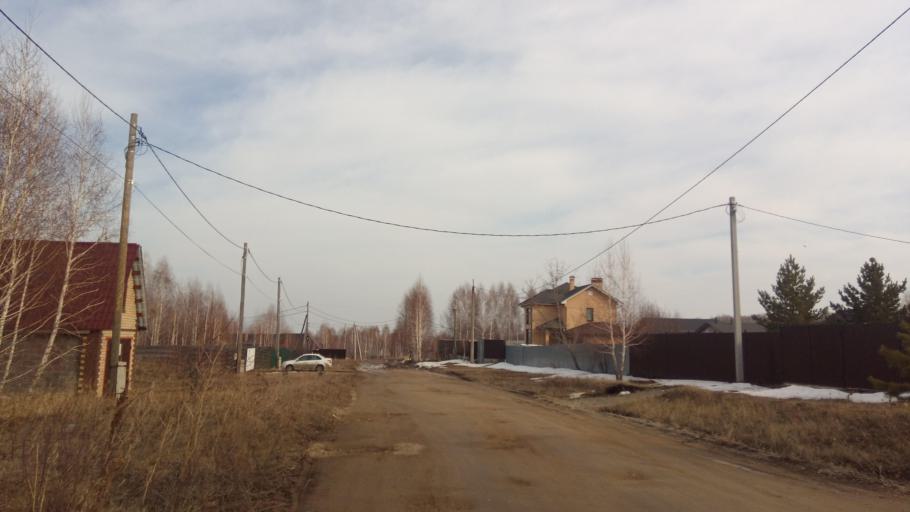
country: RU
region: Chelyabinsk
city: Sargazy
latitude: 55.1041
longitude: 61.2006
